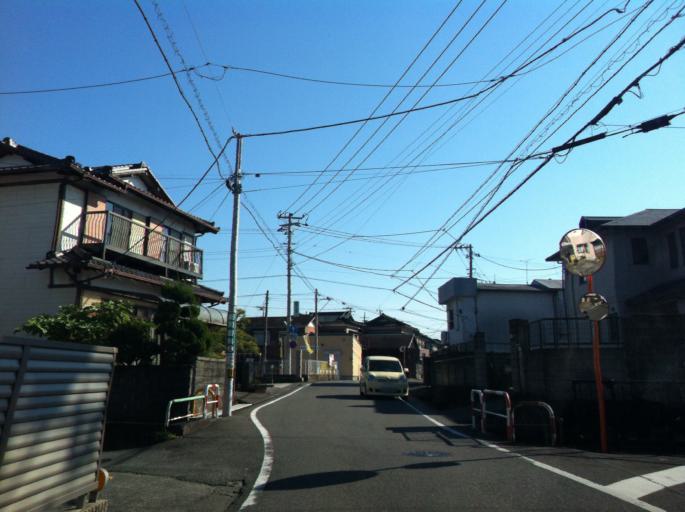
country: JP
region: Shizuoka
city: Fuji
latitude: 35.1653
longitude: 138.7236
